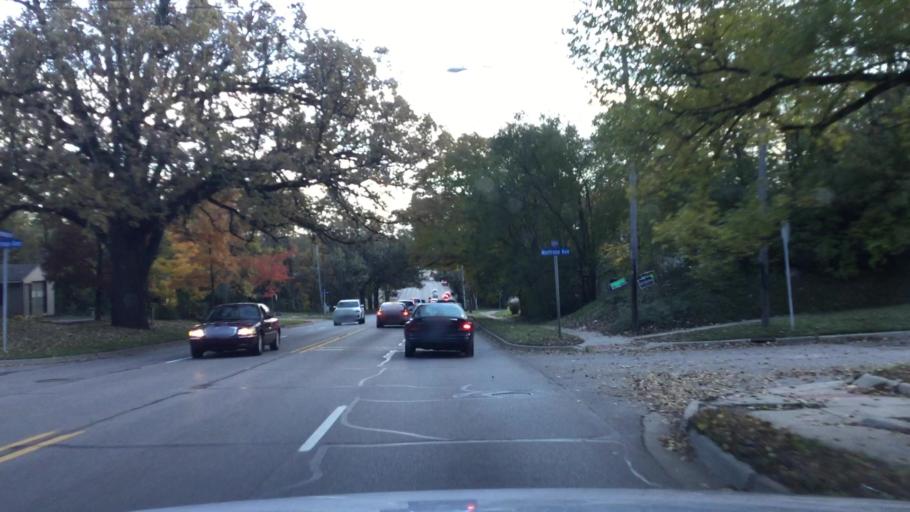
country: US
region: Michigan
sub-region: Kalamazoo County
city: Kalamazoo
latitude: 42.2644
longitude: -85.5897
